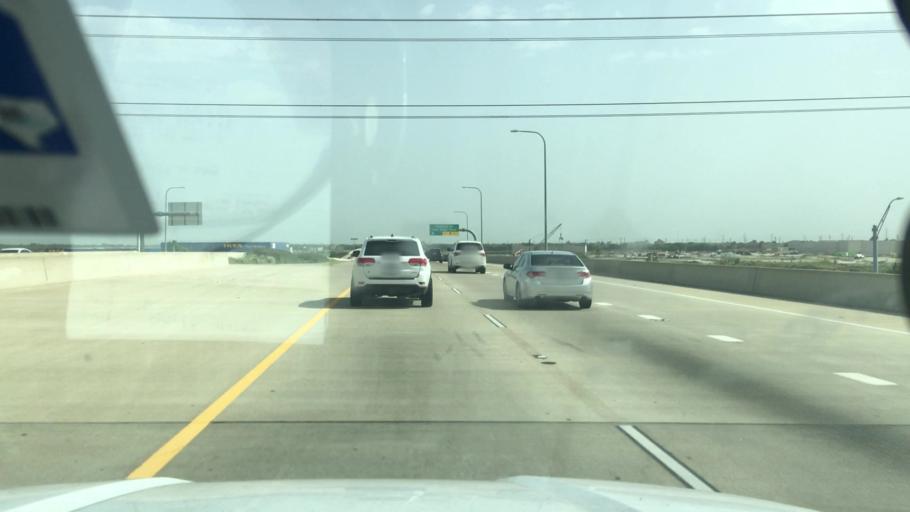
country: US
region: Texas
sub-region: Dallas County
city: Grand Prairie
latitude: 32.6988
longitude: -97.0248
